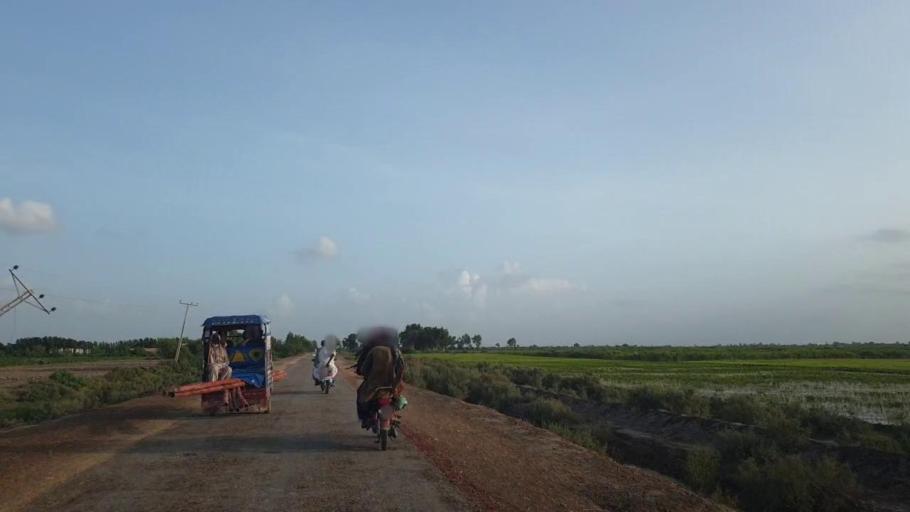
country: PK
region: Sindh
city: Kadhan
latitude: 24.6188
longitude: 69.1157
